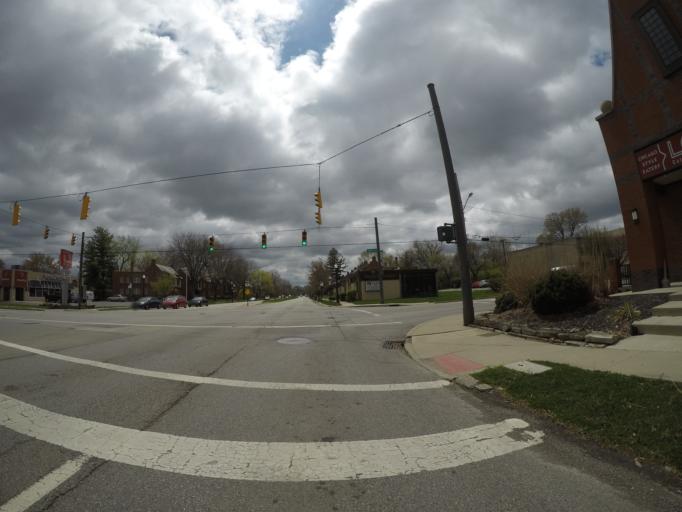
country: US
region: Ohio
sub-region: Franklin County
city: Grandview Heights
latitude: 39.9916
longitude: -83.0407
